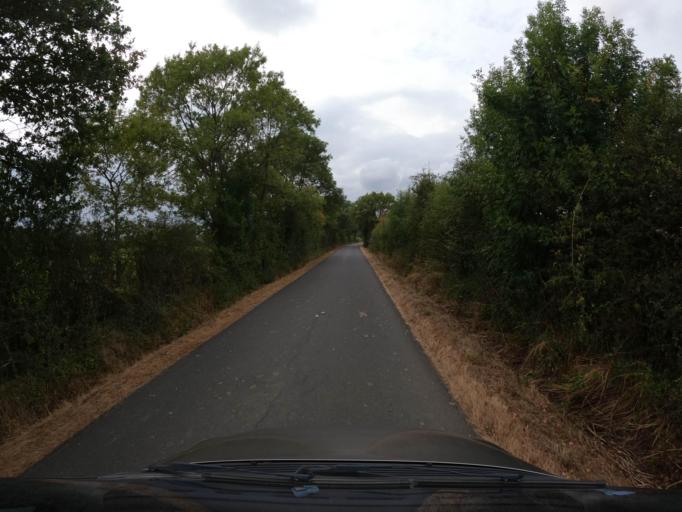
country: FR
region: Pays de la Loire
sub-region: Departement de Maine-et-Loire
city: Saint-Christophe-du-Bois
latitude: 47.0441
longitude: -0.9820
